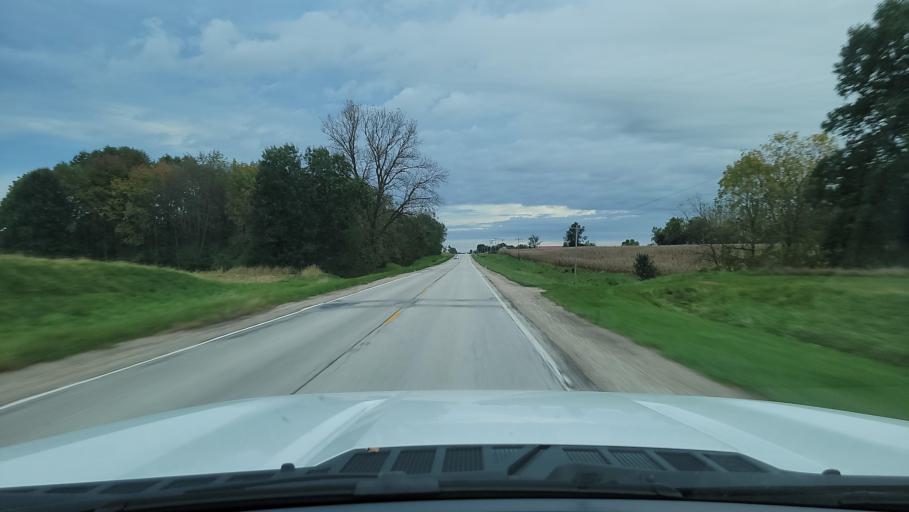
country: US
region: Illinois
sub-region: Schuyler County
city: Rushville
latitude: 40.0551
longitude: -90.6152
